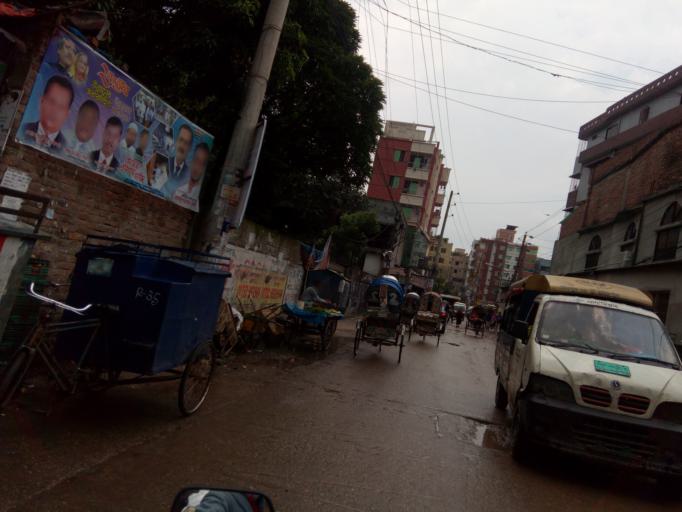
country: BD
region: Dhaka
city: Azimpur
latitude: 23.7614
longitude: 90.3590
